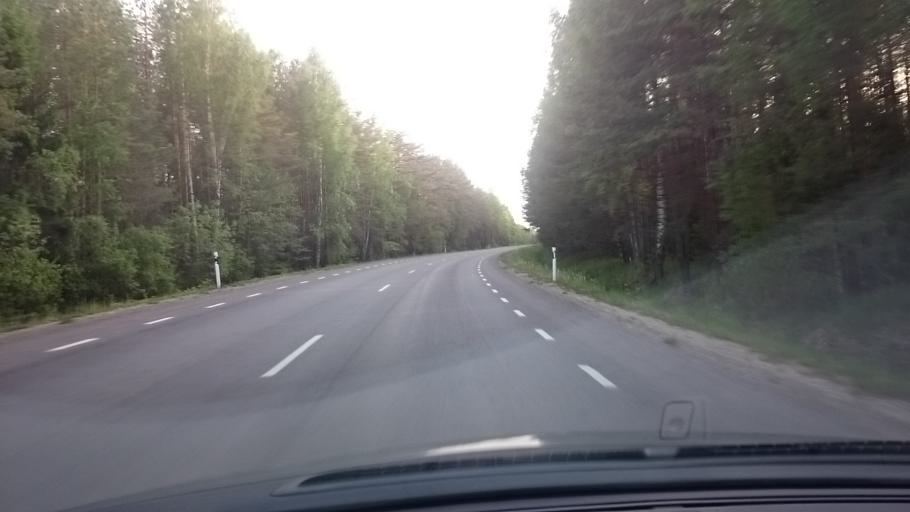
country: EE
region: Viljandimaa
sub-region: Viiratsi vald
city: Viiratsi
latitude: 58.4731
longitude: 25.7828
